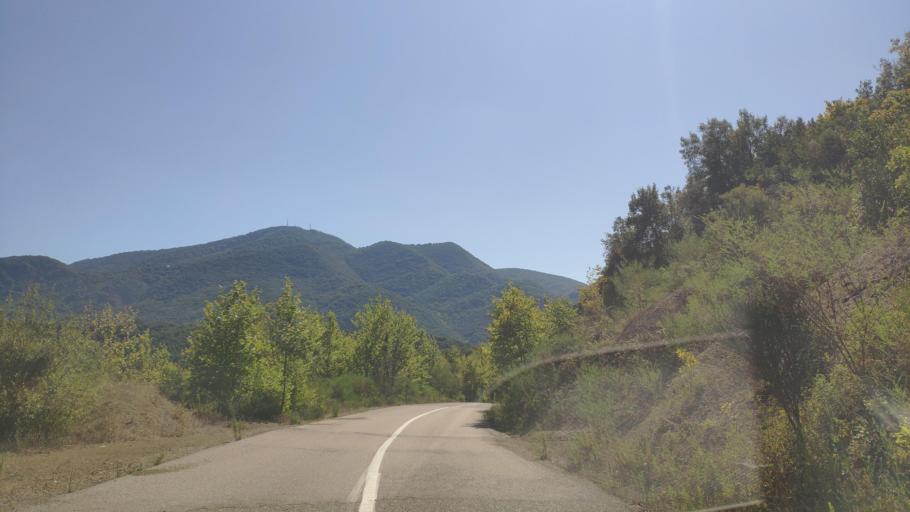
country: GR
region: Central Greece
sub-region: Nomos Evrytanias
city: Kerasochori
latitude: 38.9997
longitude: 21.5503
